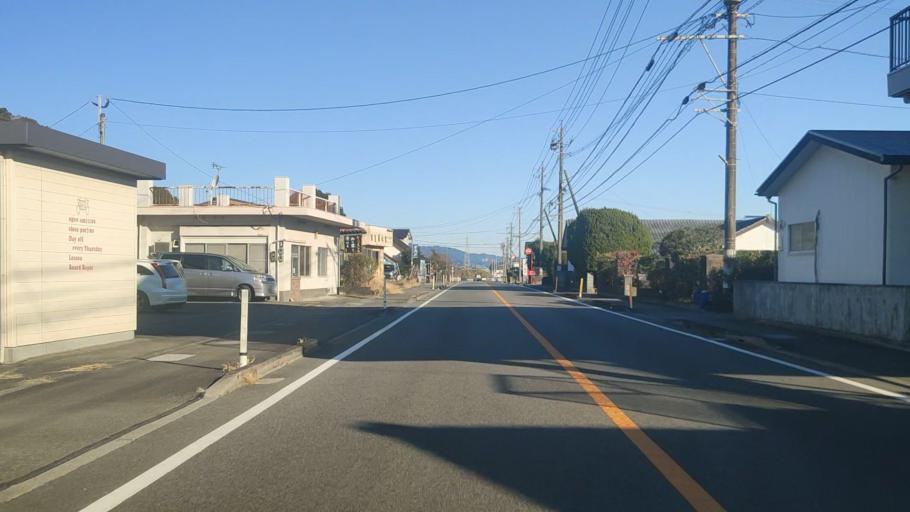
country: JP
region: Miyazaki
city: Nobeoka
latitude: 32.3860
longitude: 131.6275
